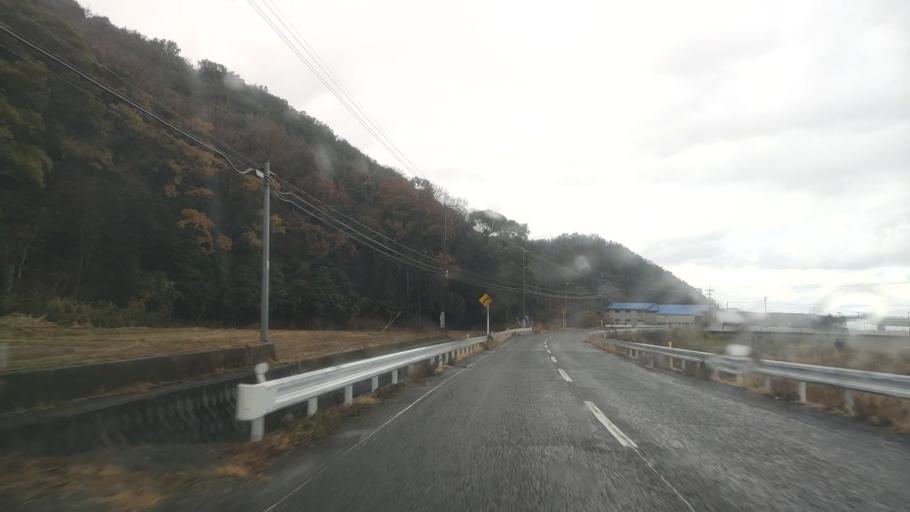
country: JP
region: Tokushima
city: Ishii
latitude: 34.2037
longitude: 134.4020
